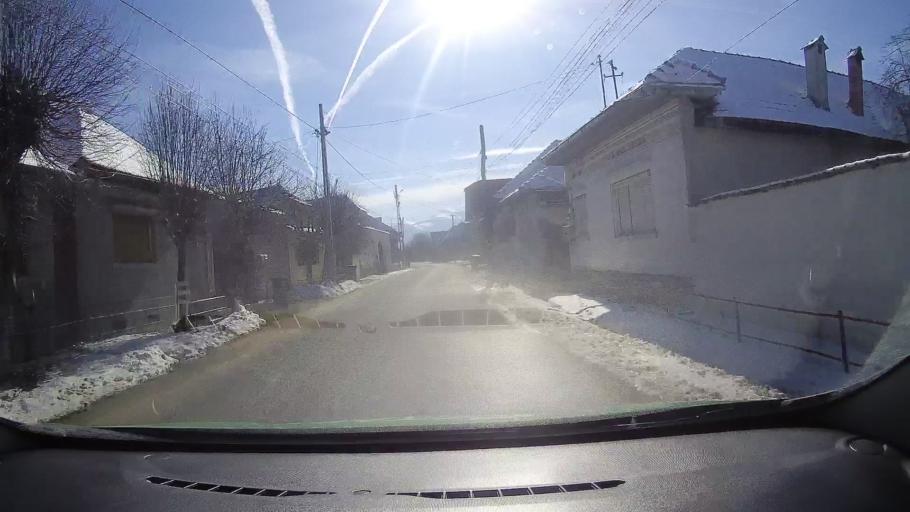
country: RO
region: Brasov
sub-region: Comuna Sambata de Sus
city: Sambata de Sus
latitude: 45.7569
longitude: 24.8306
